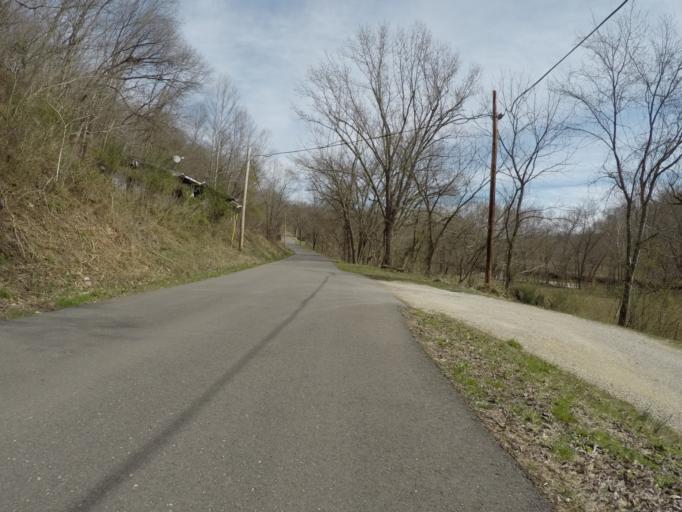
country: US
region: West Virginia
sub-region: Wayne County
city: Ceredo
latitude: 38.3733
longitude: -82.5503
